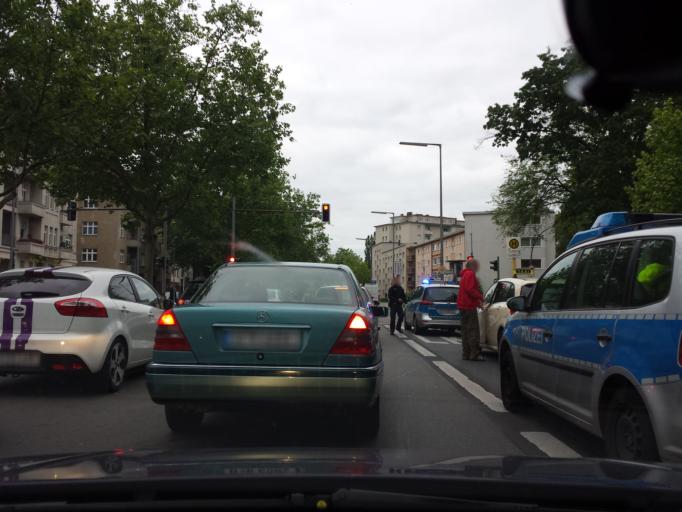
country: DE
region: Berlin
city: Spandau
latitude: 52.5287
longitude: 13.2073
